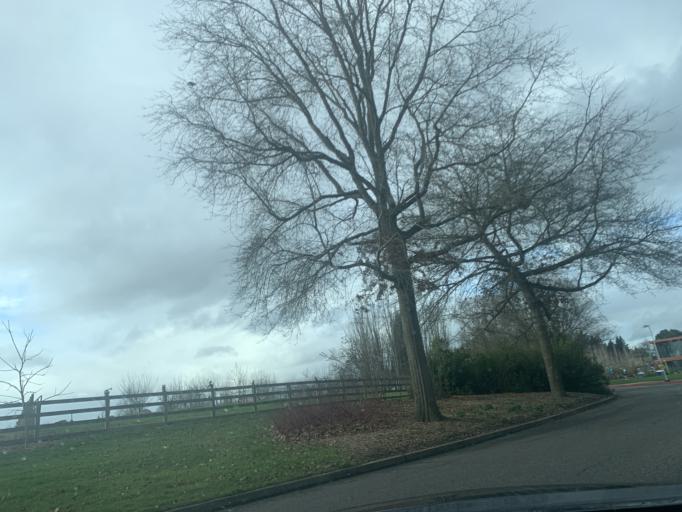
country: US
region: Oregon
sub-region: Washington County
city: Bethany
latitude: 45.5648
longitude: -122.8585
